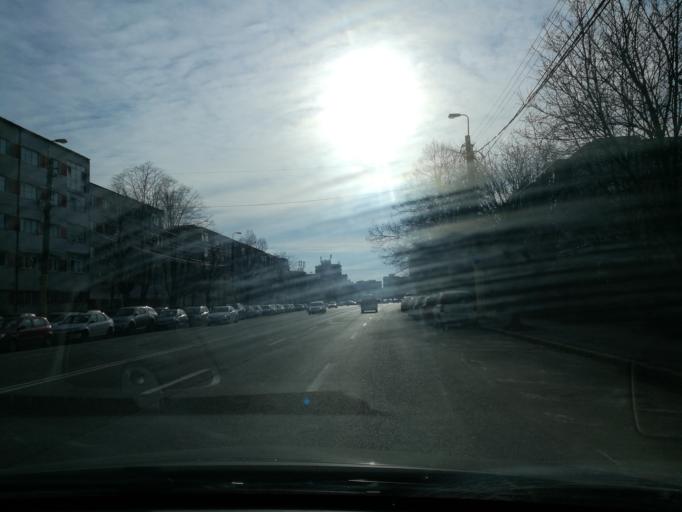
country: RO
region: Constanta
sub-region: Municipiul Constanta
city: Constanta
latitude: 44.1784
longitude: 28.6157
